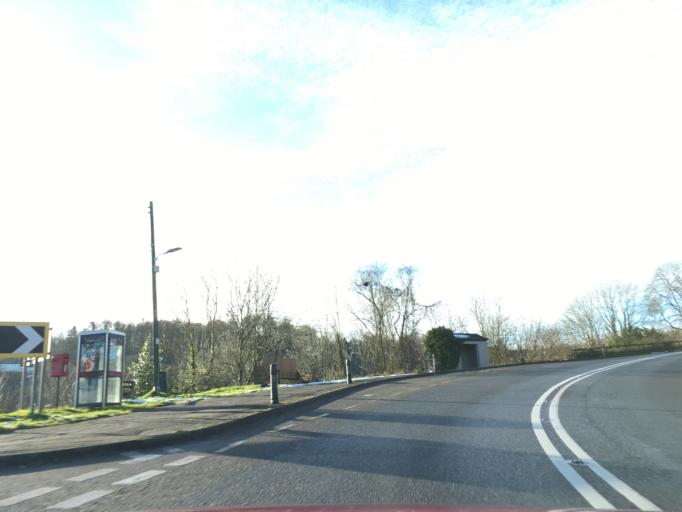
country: GB
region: England
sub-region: Gloucestershire
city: Mitcheldean
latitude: 51.8520
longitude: -2.4889
